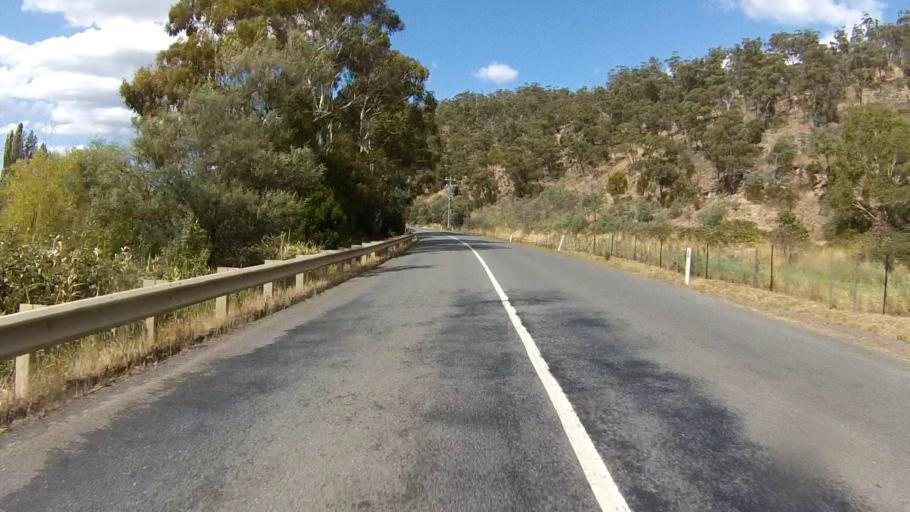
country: AU
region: Tasmania
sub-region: Derwent Valley
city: New Norfolk
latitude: -42.7771
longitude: 147.0288
